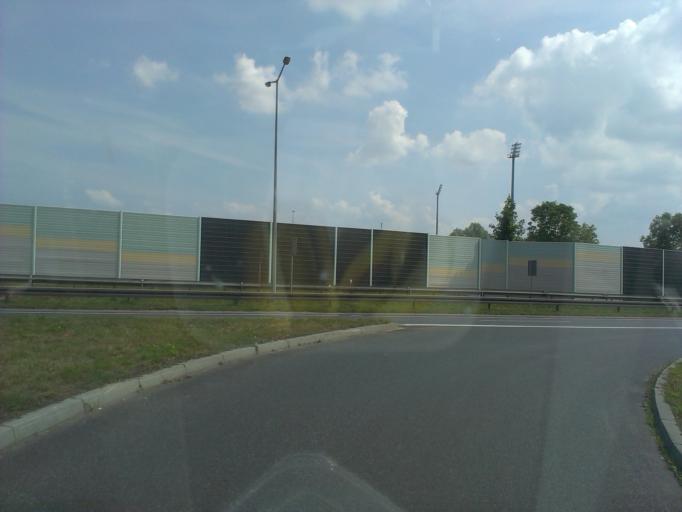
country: PL
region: Lower Silesian Voivodeship
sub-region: Powiat polkowicki
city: Polkowice
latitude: 51.5011
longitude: 16.0616
